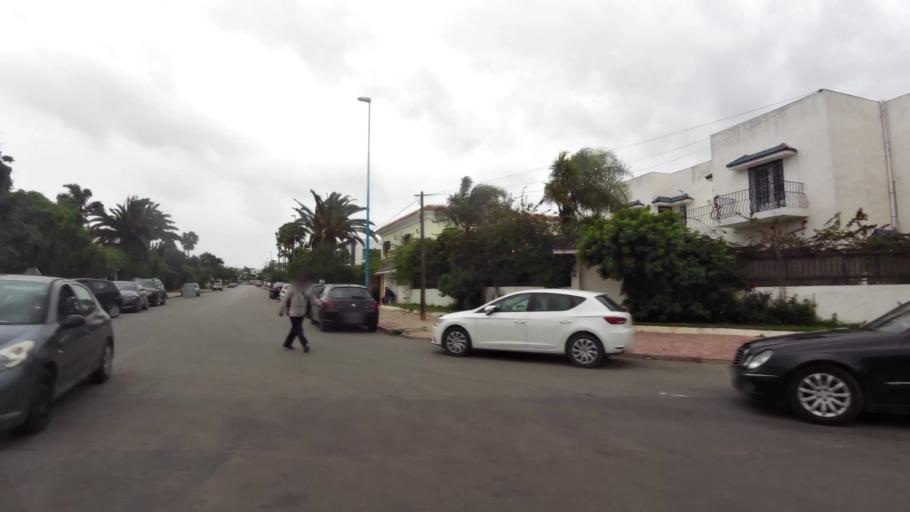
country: MA
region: Grand Casablanca
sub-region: Casablanca
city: Casablanca
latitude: 33.5958
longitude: -7.6548
